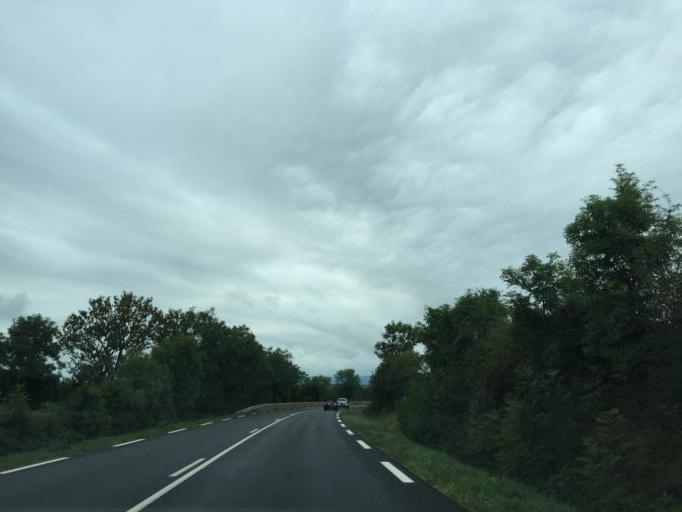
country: FR
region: Midi-Pyrenees
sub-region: Departement de l'Aveyron
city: Bozouls
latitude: 44.4908
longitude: 2.7386
